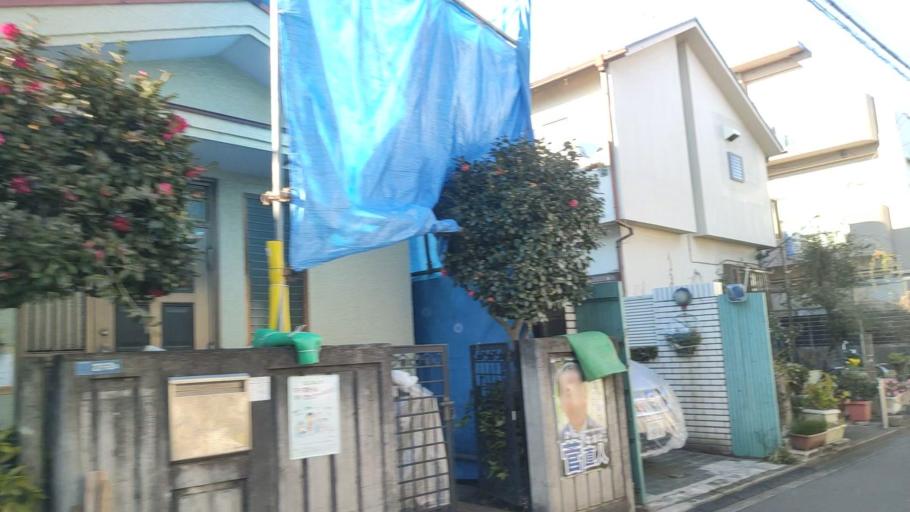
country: JP
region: Tokyo
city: Musashino
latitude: 35.7071
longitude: 139.5711
